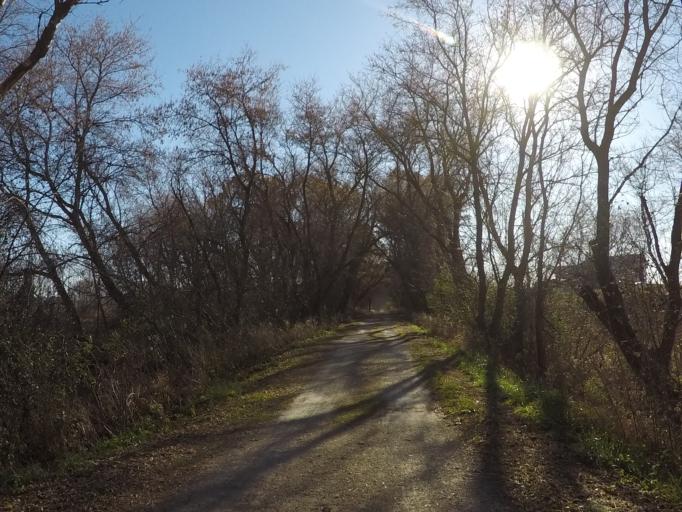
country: US
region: Wisconsin
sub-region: Dane County
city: Deerfield
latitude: 43.0493
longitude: -89.0607
